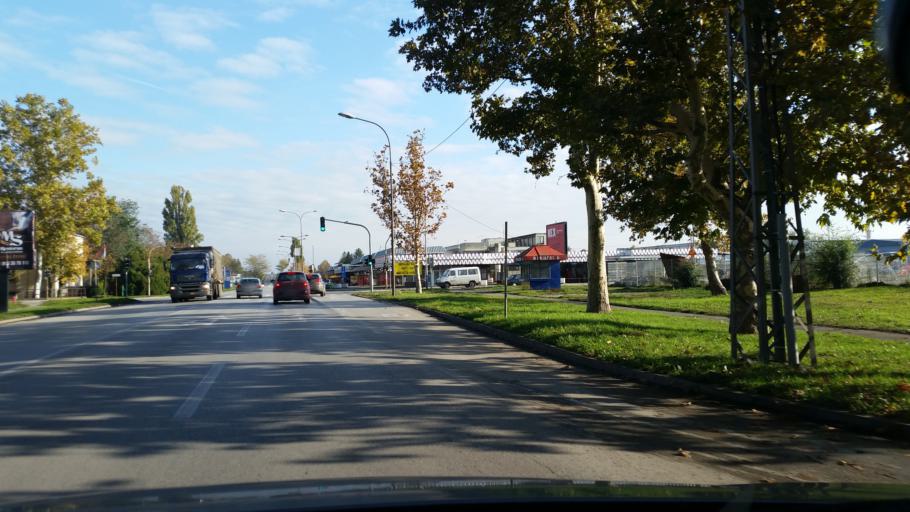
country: RS
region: Autonomna Pokrajina Vojvodina
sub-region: Srednjebanatski Okrug
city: Zrenjanin
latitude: 45.3741
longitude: 20.4130
